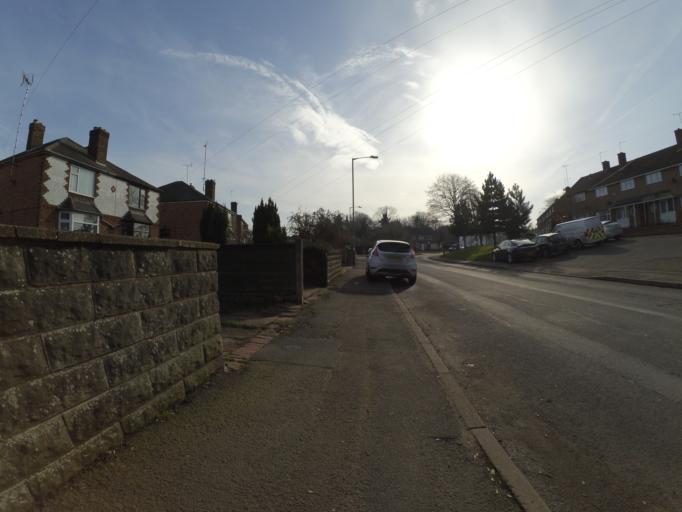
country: GB
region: England
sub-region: Warwickshire
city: Rugby
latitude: 52.3629
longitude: -1.2166
